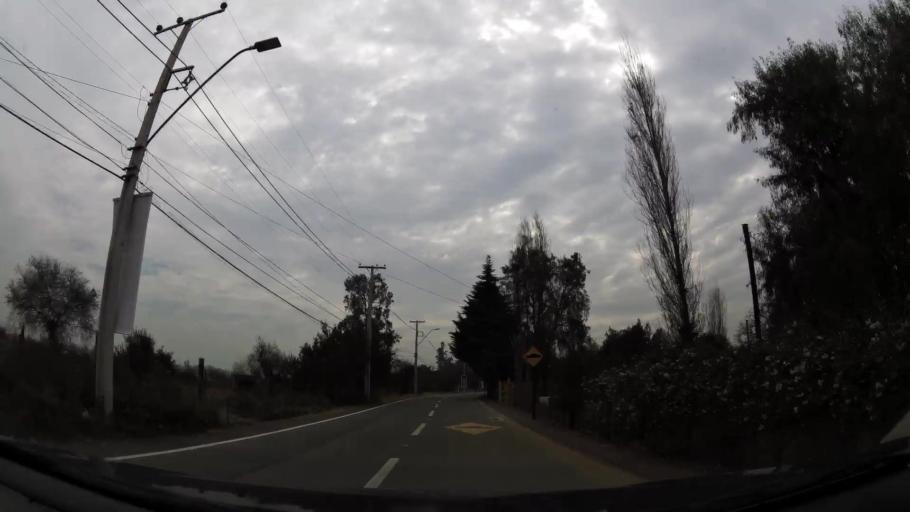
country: CL
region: Santiago Metropolitan
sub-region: Provincia de Chacabuco
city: Chicureo Abajo
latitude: -33.2134
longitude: -70.6619
